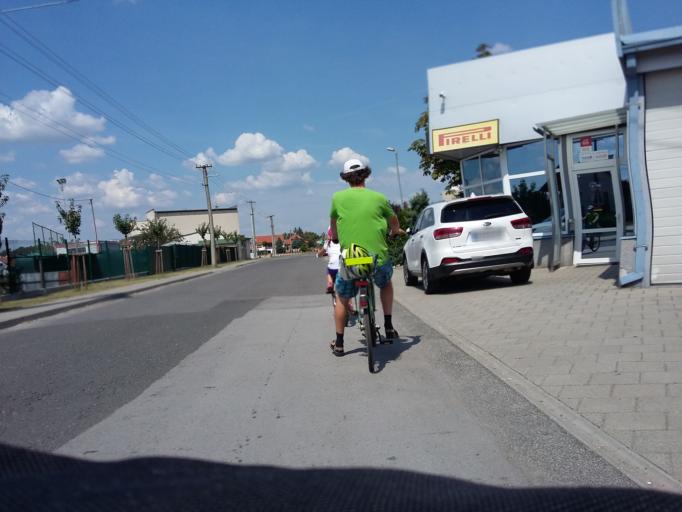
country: SK
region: Bratislavsky
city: Stupava
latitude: 48.3341
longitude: 17.0411
